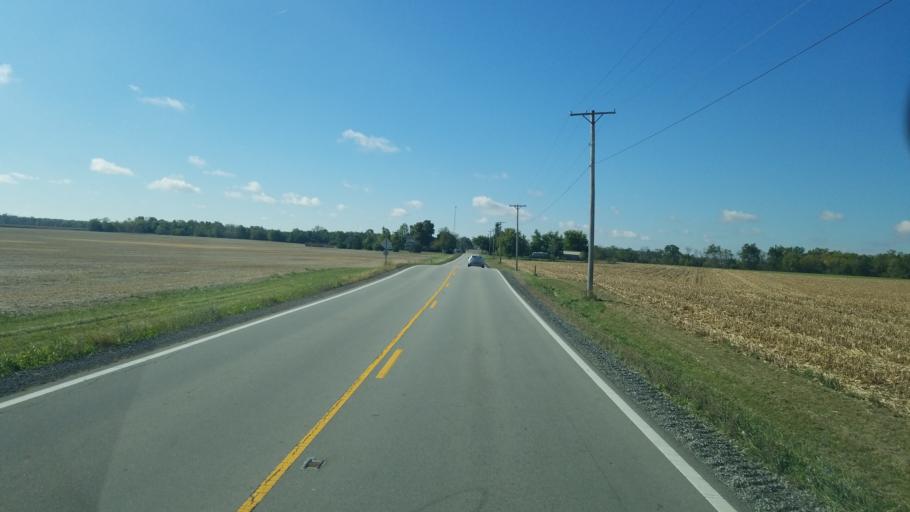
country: US
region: Ohio
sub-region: Fayette County
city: Washington Court House
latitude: 39.4458
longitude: -83.5035
